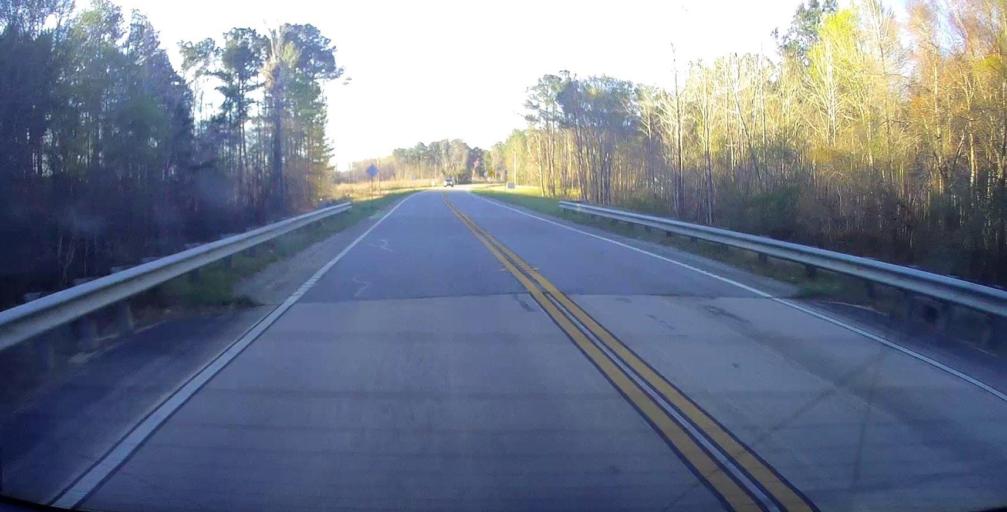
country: US
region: Georgia
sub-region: Wilcox County
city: Abbeville
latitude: 32.0144
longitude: -83.2491
